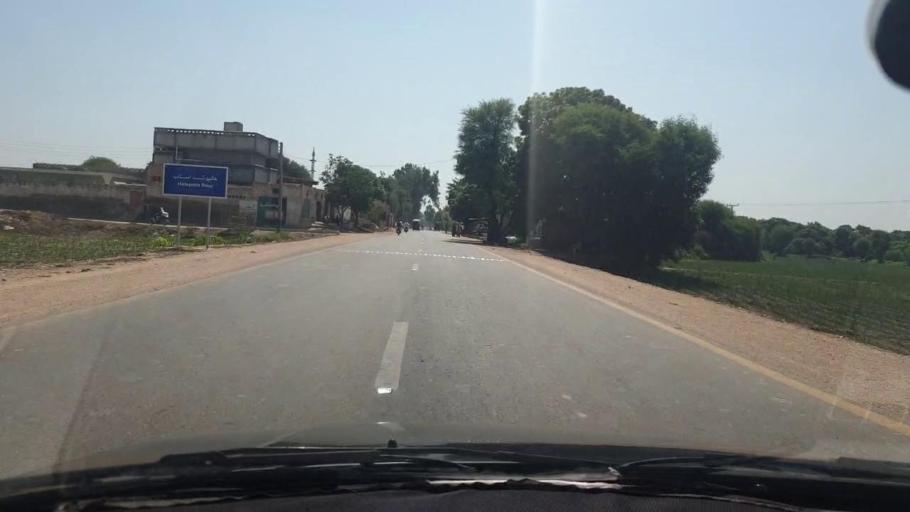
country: PK
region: Sindh
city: Tando Allahyar
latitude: 25.4265
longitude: 68.7508
